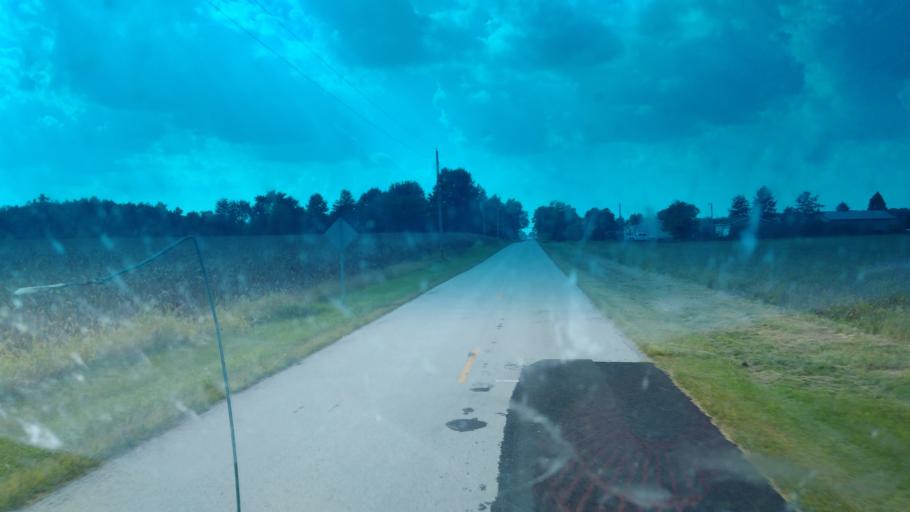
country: US
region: Ohio
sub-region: Hardin County
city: Kenton
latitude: 40.7460
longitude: -83.6129
